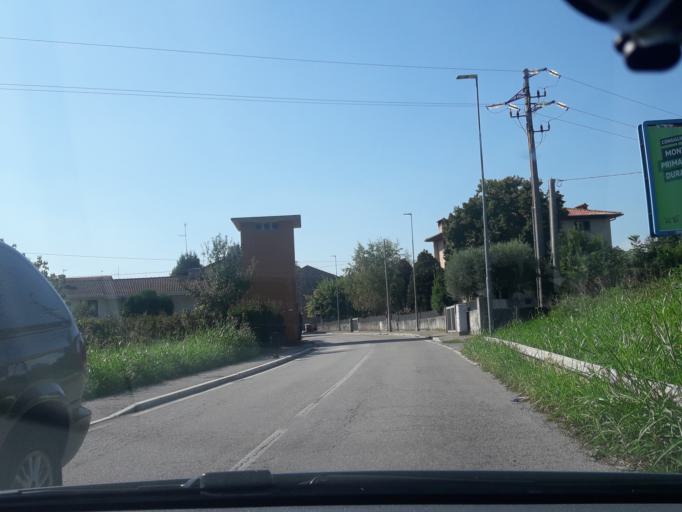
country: IT
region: Friuli Venezia Giulia
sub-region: Provincia di Udine
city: Passons
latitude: 46.0574
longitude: 13.2065
